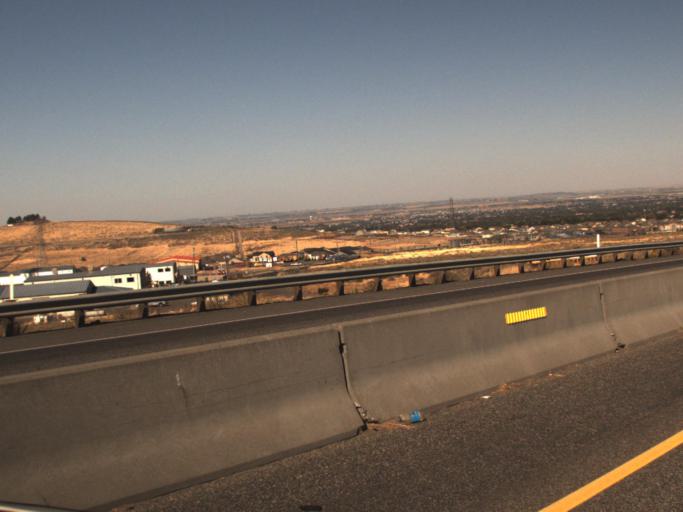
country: US
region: Washington
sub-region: Benton County
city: Kennewick
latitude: 46.1661
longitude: -119.2018
